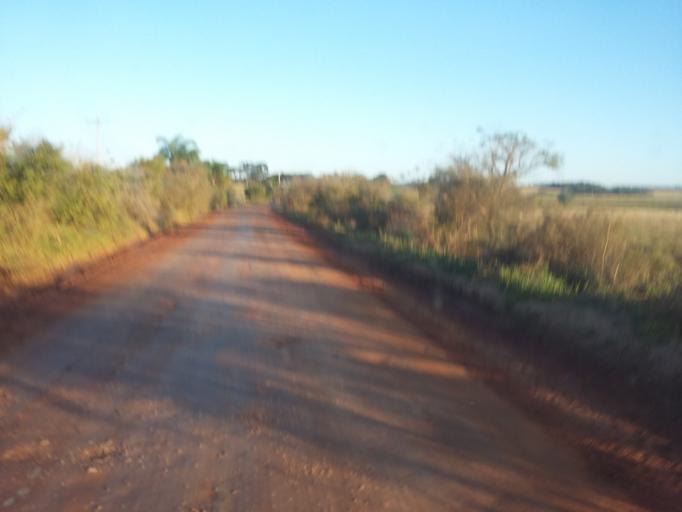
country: BR
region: Rio Grande do Sul
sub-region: Camaqua
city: Camaqua
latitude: -30.7455
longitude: -51.7736
